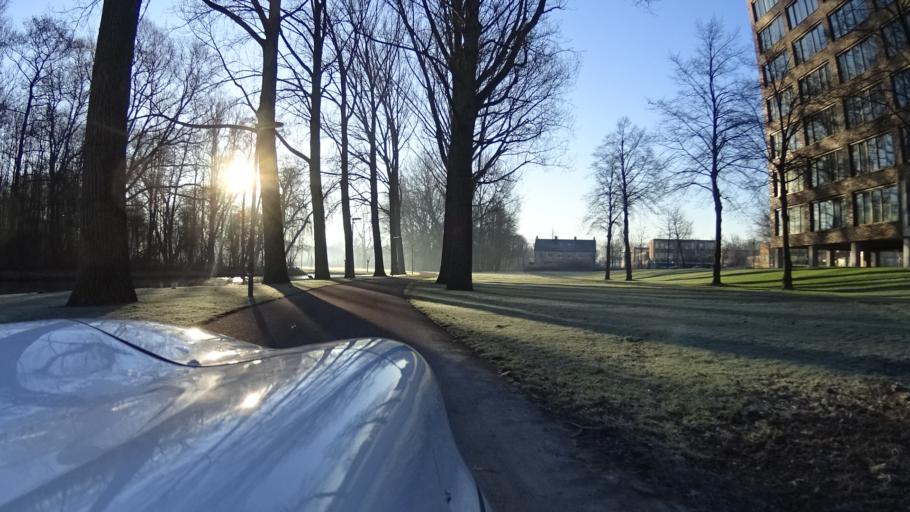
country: NL
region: South Holland
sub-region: Gemeente Barendrecht
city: Barendrecht
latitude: 51.8745
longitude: 4.5003
